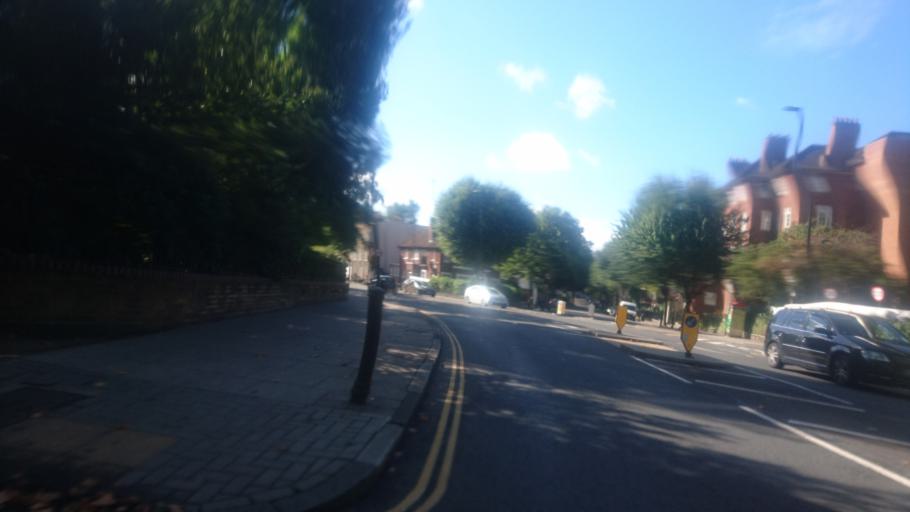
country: GB
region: England
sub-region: Greater London
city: Islington
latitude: 51.5431
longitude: -0.1001
